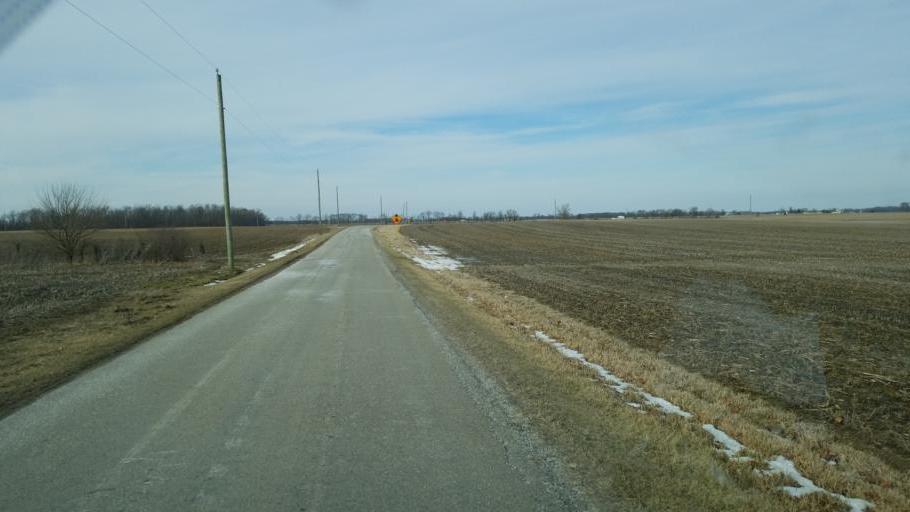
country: US
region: Ohio
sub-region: Union County
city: Marysville
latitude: 40.3058
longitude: -83.3139
